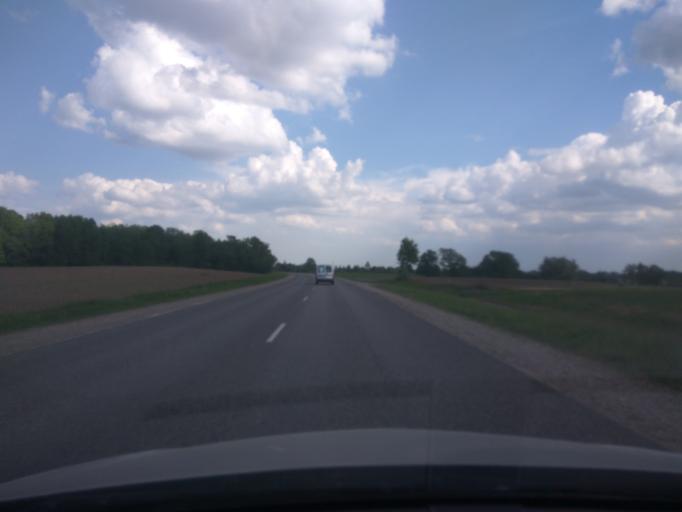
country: LV
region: Kuldigas Rajons
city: Kuldiga
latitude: 56.9875
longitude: 21.9213
